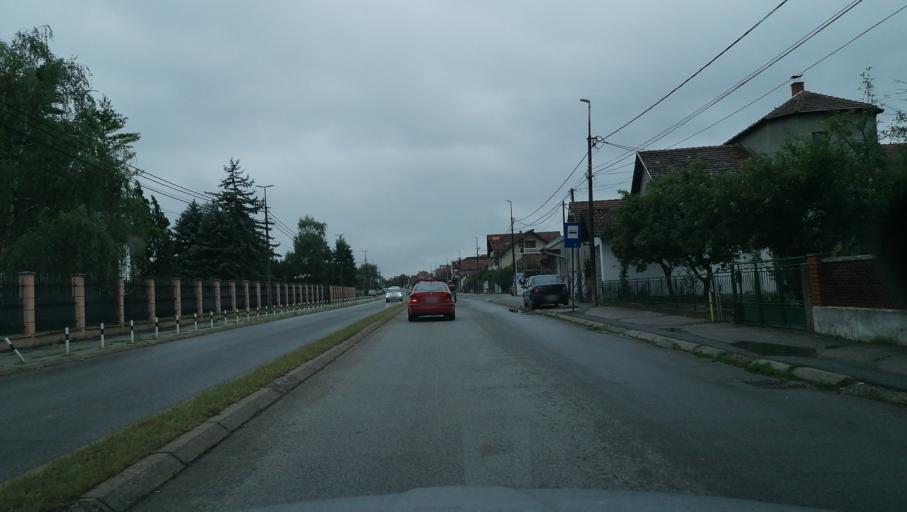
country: RS
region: Central Serbia
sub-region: Rasinski Okrug
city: Krusevac
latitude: 43.5851
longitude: 21.3018
